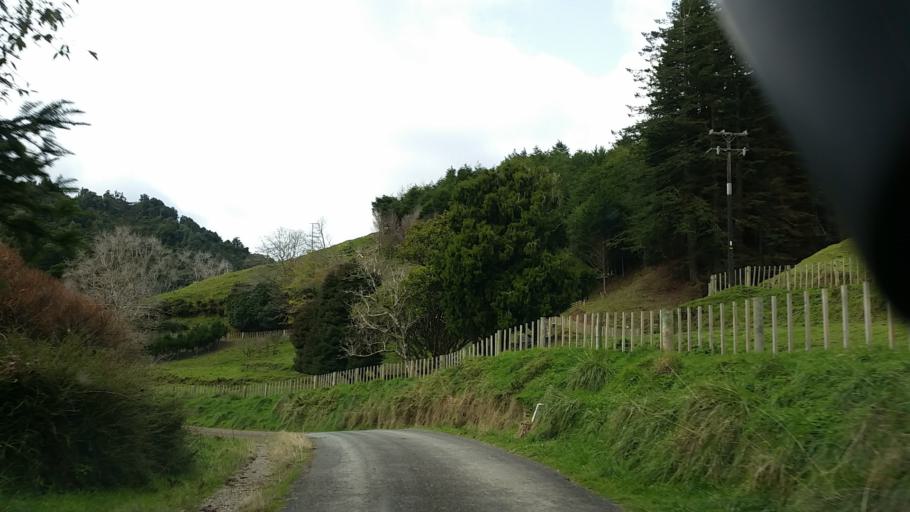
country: NZ
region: Taranaki
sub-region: New Plymouth District
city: Waitara
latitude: -39.0370
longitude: 174.5838
